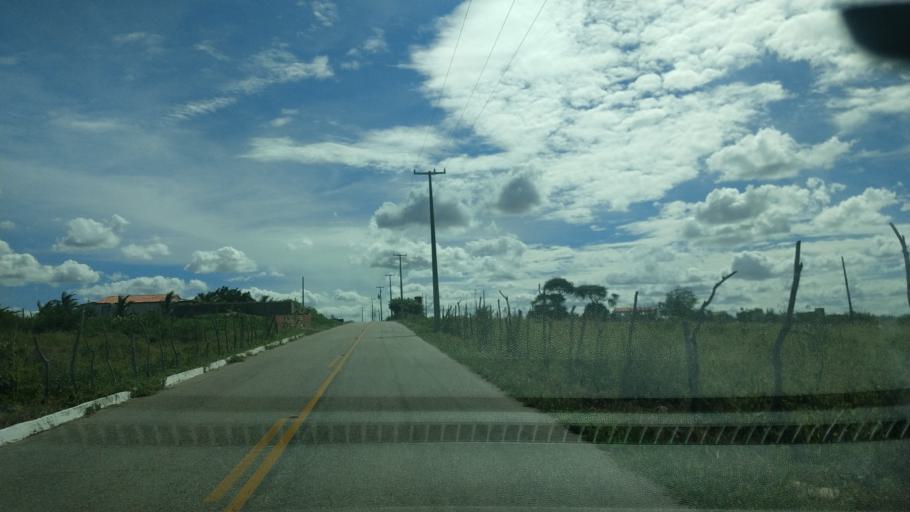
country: BR
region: Rio Grande do Norte
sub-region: Sao Jose Do Campestre
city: Sao Jose do Campestre
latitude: -6.4211
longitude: -35.7526
